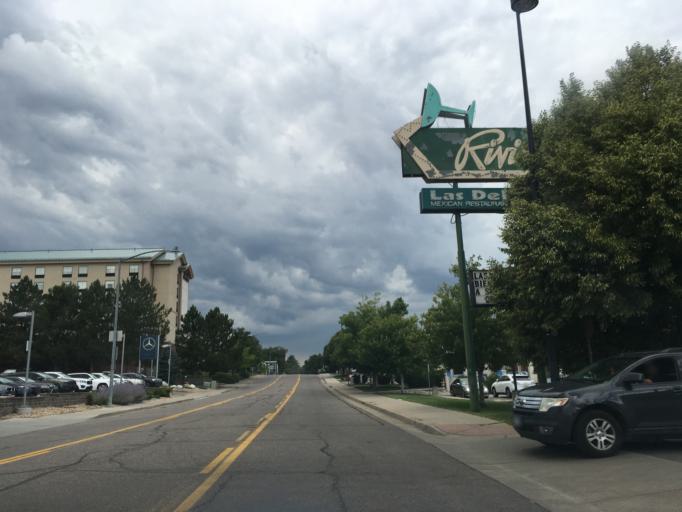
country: US
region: Colorado
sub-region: Arapahoe County
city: Glendale
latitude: 39.7003
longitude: -104.9375
